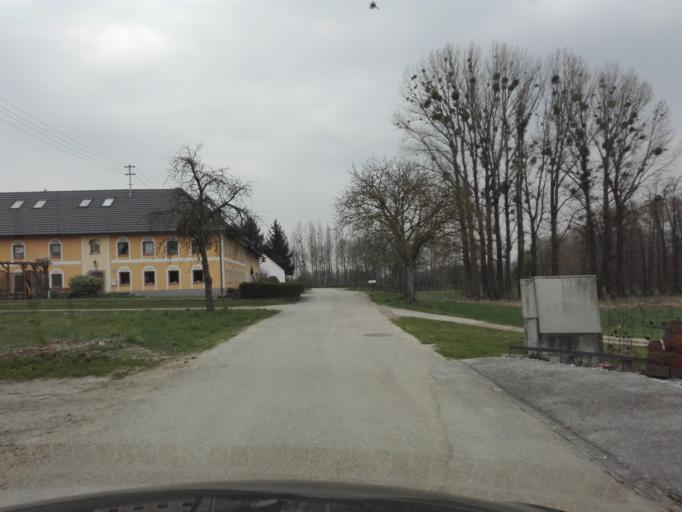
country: AT
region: Upper Austria
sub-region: Politischer Bezirk Perg
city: Perg
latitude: 48.2443
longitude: 14.5953
